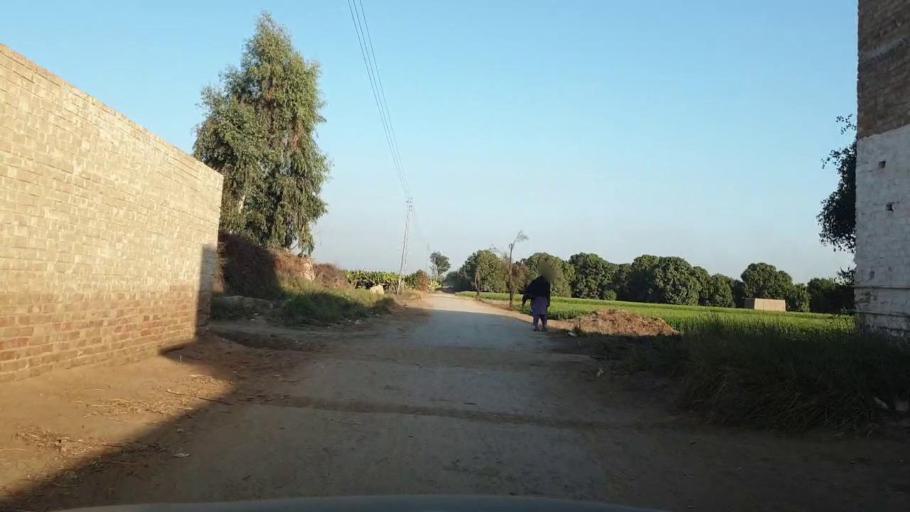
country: PK
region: Sindh
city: Matiari
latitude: 25.6168
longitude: 68.6008
